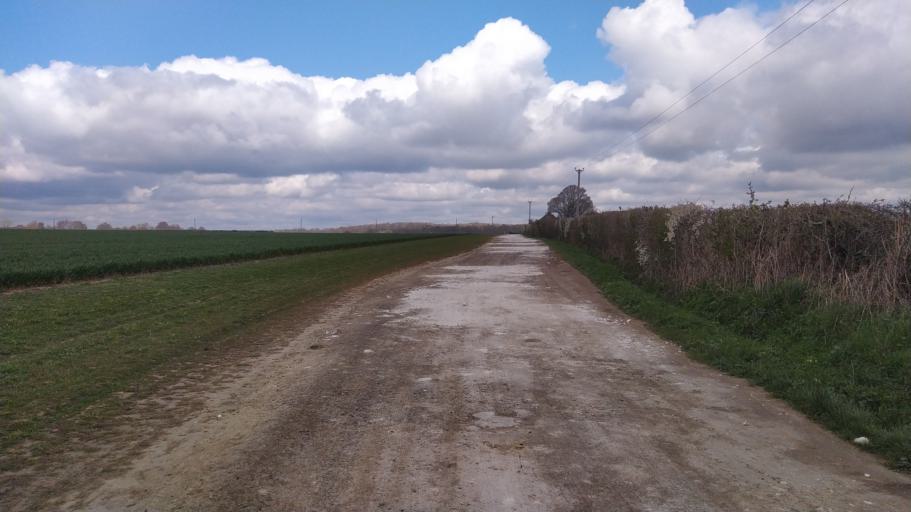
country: GB
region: England
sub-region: West Sussex
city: Petworth
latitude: 51.0218
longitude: -0.5768
